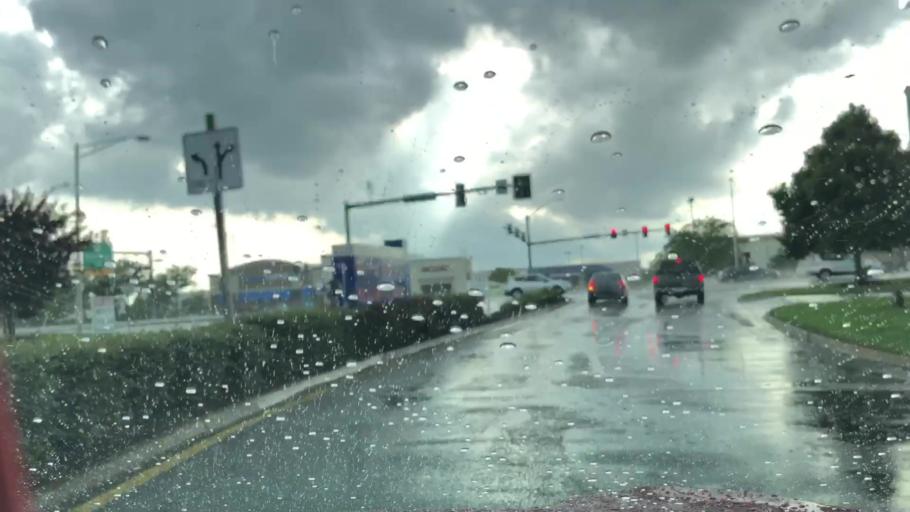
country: US
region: Virginia
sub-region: City of Chesapeake
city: Chesapeake
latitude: 36.8588
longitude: -76.2093
